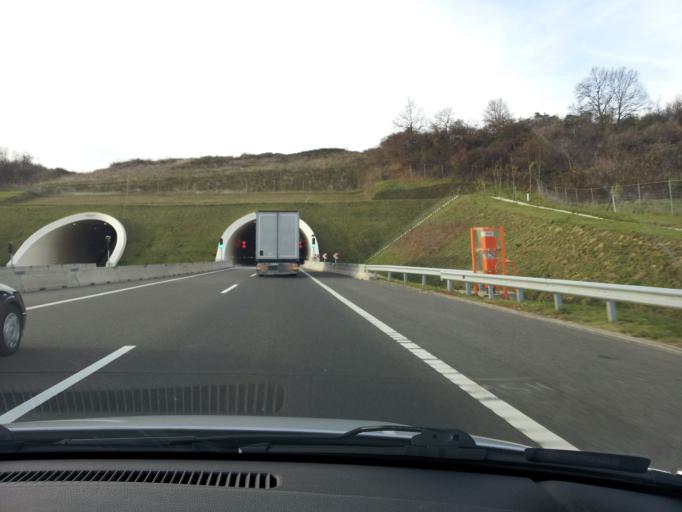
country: HU
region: Tolna
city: Bataszek
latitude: 46.1595
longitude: 18.6555
